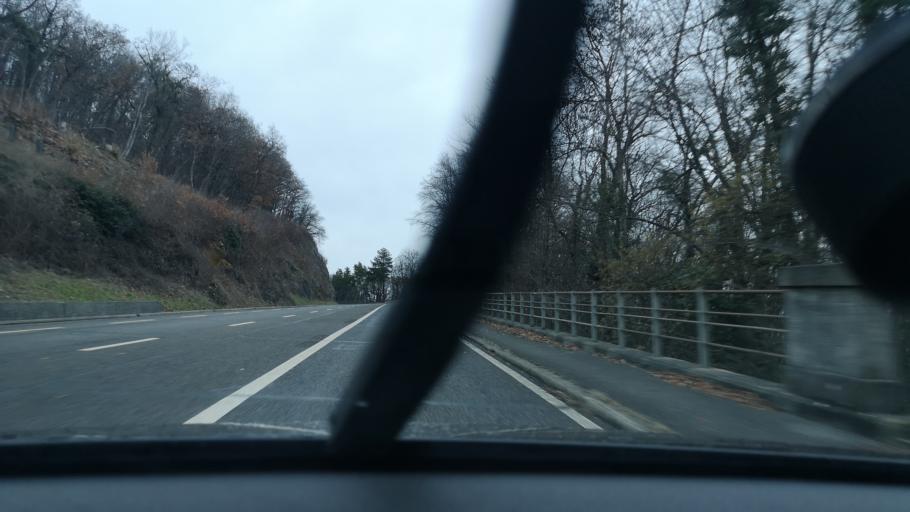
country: CH
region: Neuchatel
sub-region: Boudry District
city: Saint-Aubin-Sauges
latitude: 46.8605
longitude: 6.7344
